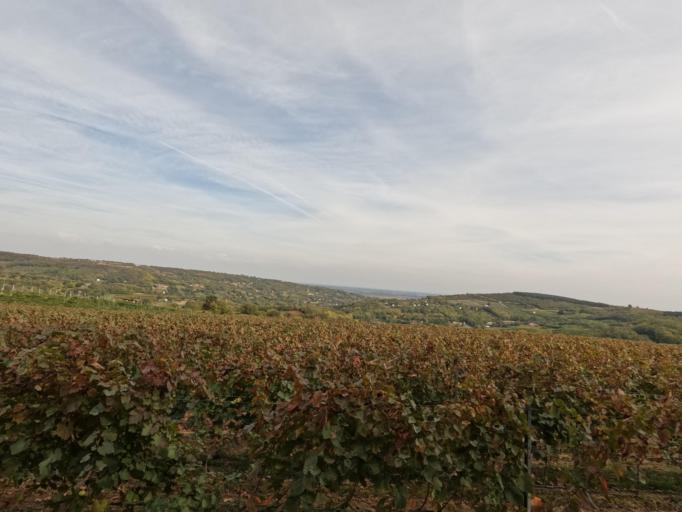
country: HU
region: Tolna
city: Szentgalpuszta
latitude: 46.3308
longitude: 18.6525
